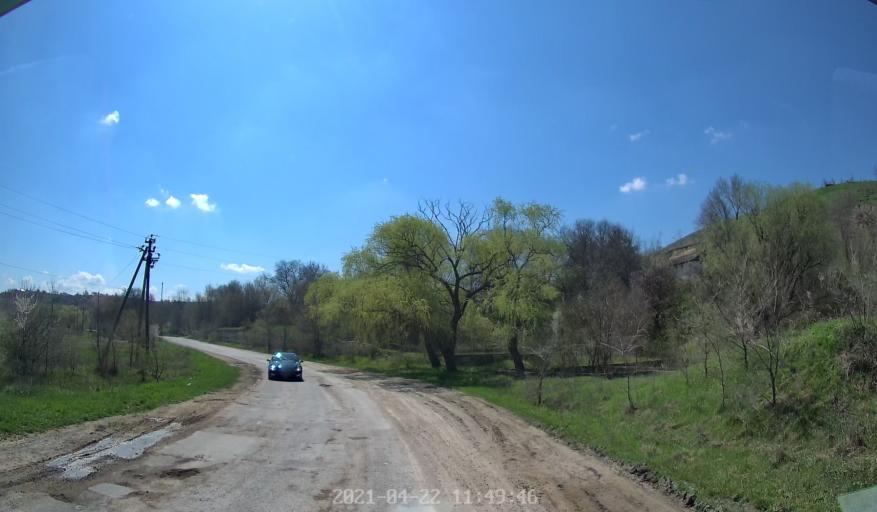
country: MD
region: Chisinau
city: Ciorescu
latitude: 47.1409
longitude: 28.8970
